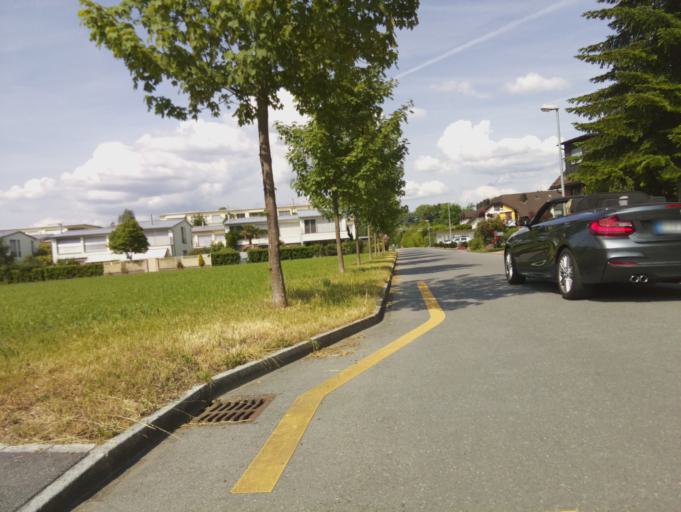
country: CH
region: Schwyz
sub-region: Bezirk March
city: Lachen
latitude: 47.1953
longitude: 8.8610
